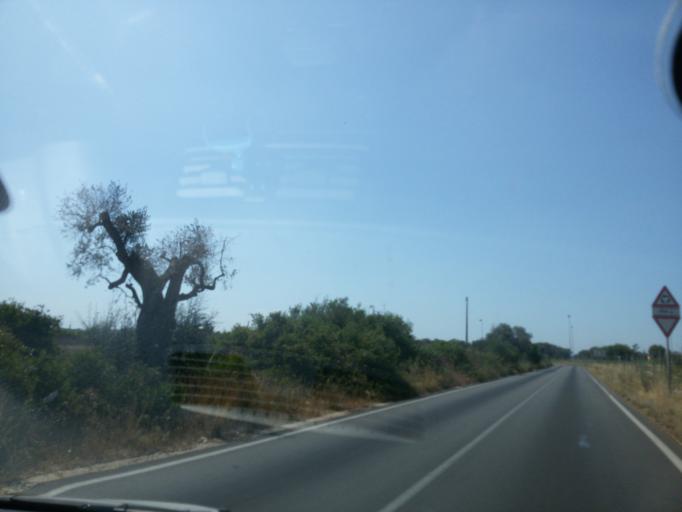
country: IT
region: Apulia
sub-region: Provincia di Lecce
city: Porto Cesareo
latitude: 40.2226
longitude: 17.9407
